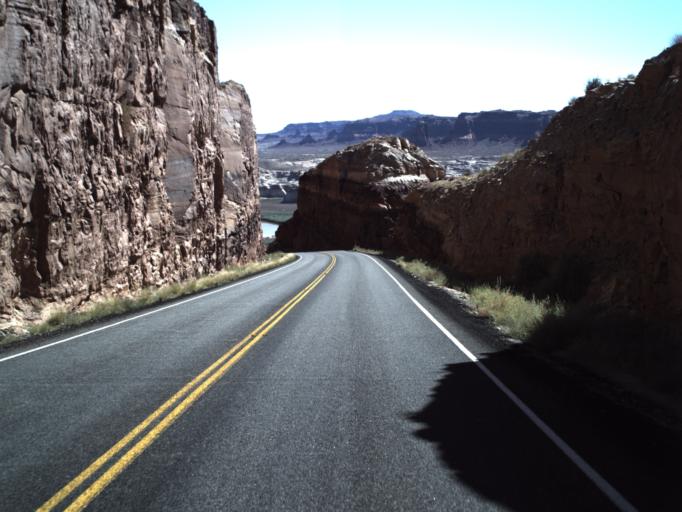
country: US
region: Utah
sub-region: San Juan County
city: Blanding
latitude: 37.8898
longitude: -110.4116
